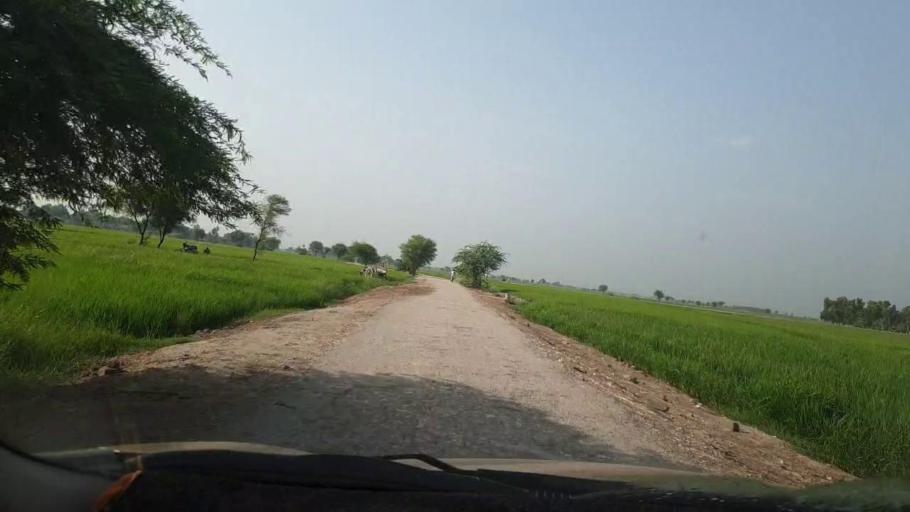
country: PK
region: Sindh
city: Goth Garelo
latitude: 27.4680
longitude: 68.0891
